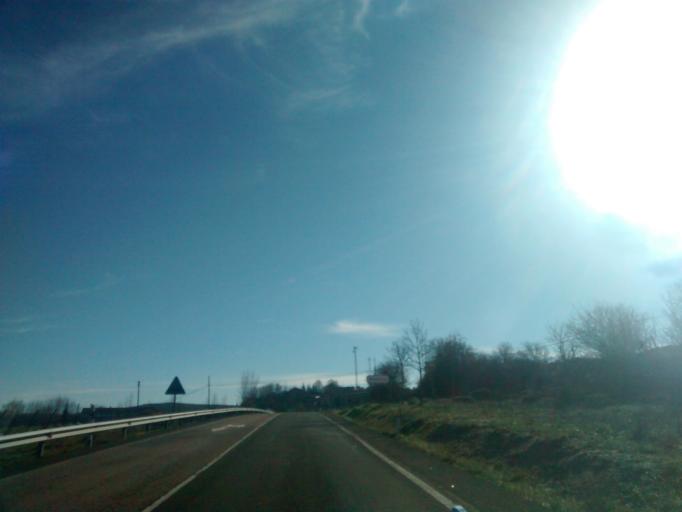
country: ES
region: Cantabria
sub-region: Provincia de Cantabria
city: San Pedro del Romeral
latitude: 42.9733
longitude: -3.7938
